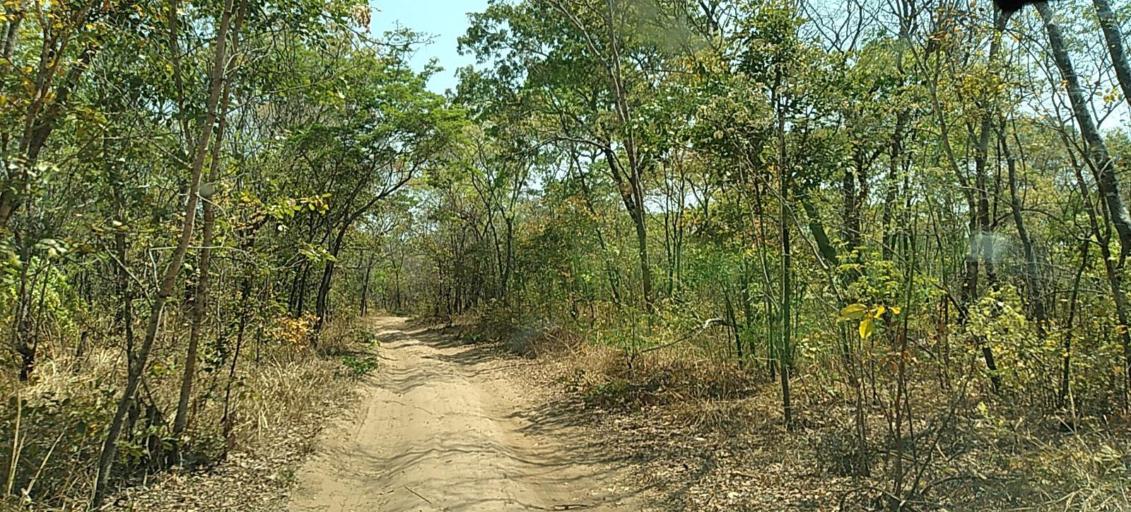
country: ZM
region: North-Western
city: Kalengwa
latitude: -13.1152
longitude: 24.6905
